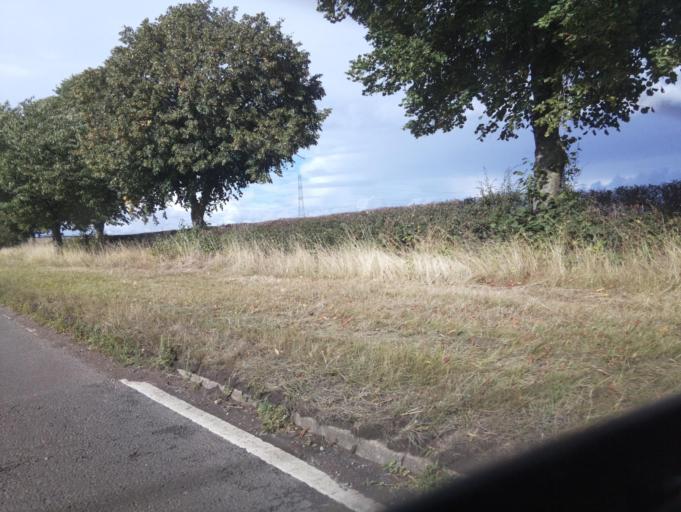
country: GB
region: England
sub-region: Telford and Wrekin
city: Madeley
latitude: 52.6026
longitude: -2.4045
